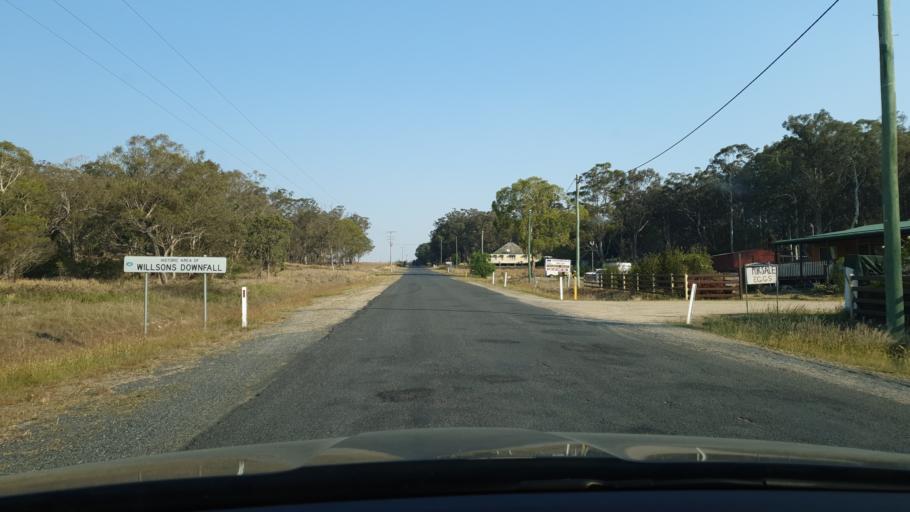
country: AU
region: New South Wales
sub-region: Tenterfield Municipality
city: Carrolls Creek
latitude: -28.6889
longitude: 152.0857
